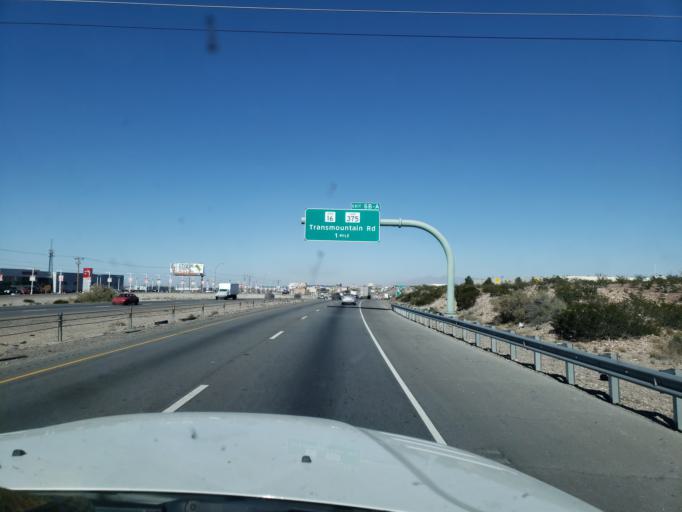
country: US
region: Texas
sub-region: El Paso County
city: Canutillo
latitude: 31.8859
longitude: -106.5825
